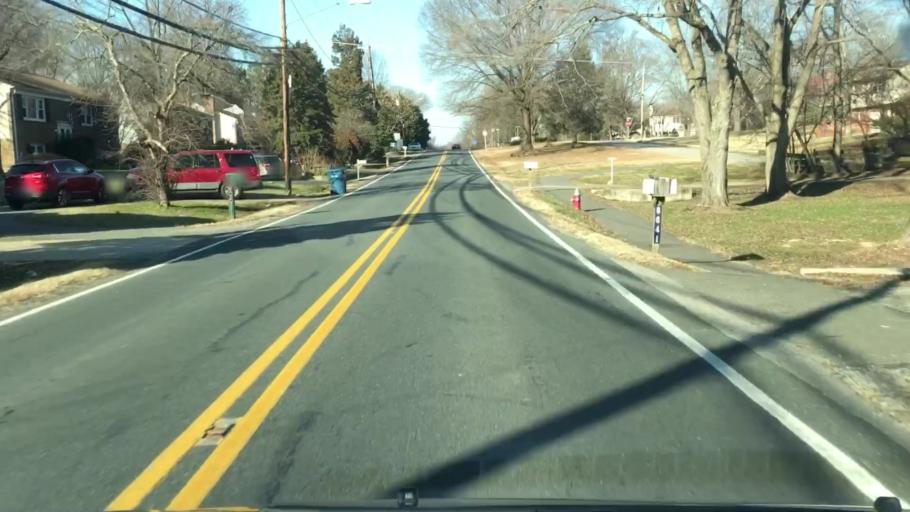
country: US
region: Virginia
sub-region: Fairfax County
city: Mount Vernon
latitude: 38.7224
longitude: -77.0902
